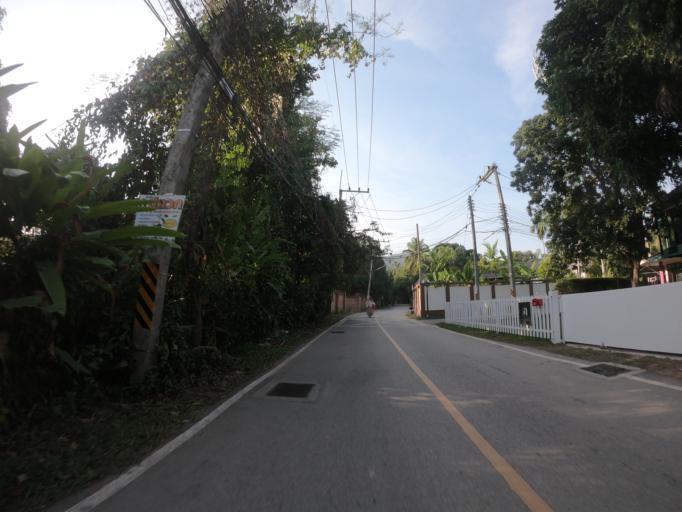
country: TH
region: Chiang Mai
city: Chiang Mai
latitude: 18.8177
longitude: 98.9541
